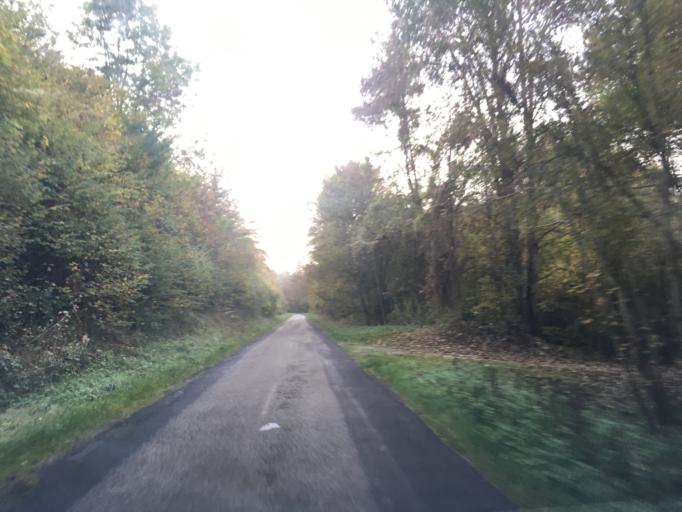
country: FR
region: Haute-Normandie
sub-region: Departement de l'Eure
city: Heudreville-sur-Eure
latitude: 49.1048
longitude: 1.2259
